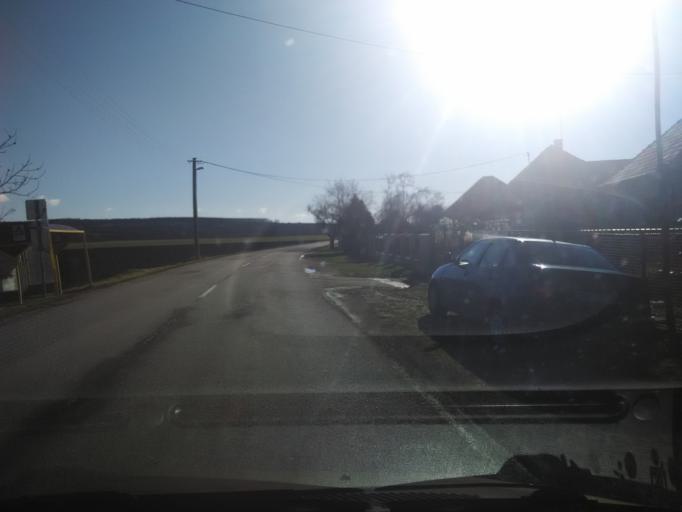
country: SK
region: Nitriansky
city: Surany
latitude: 48.1810
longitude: 18.2149
